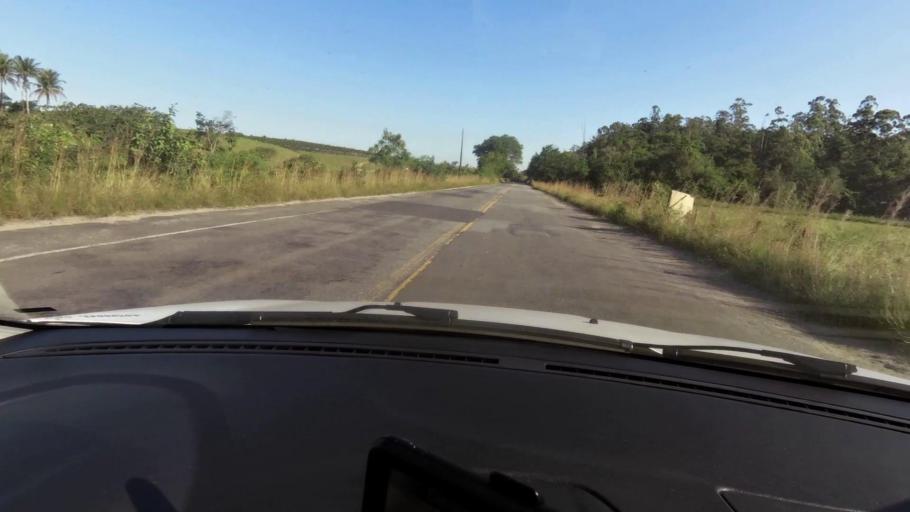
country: BR
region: Espirito Santo
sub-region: Piuma
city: Piuma
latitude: -20.7422
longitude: -40.6477
